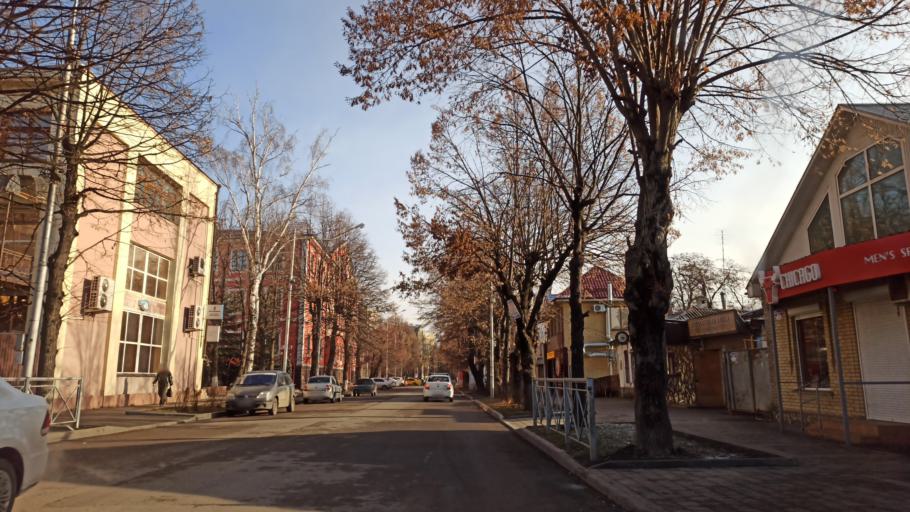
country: RU
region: Stavropol'skiy
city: Yessentuki
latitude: 44.0427
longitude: 42.8549
